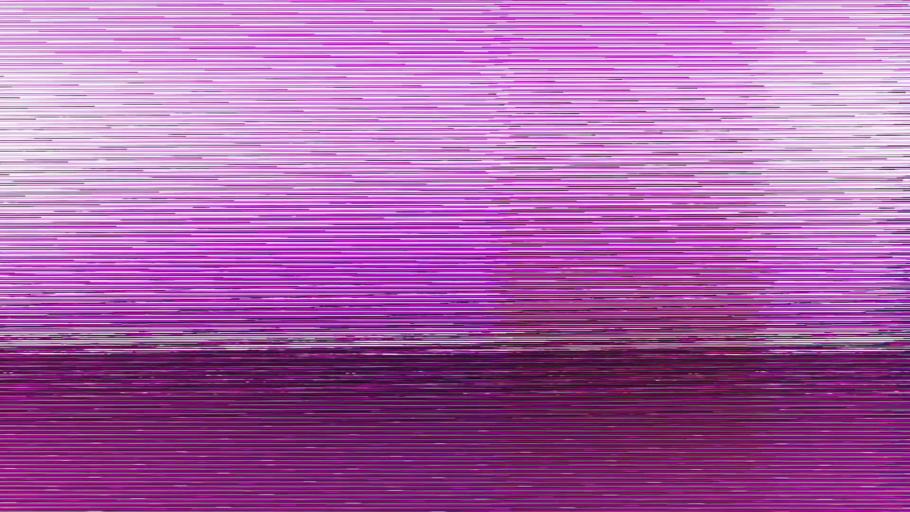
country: US
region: Michigan
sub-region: Livingston County
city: Brighton
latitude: 42.6267
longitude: -83.7486
